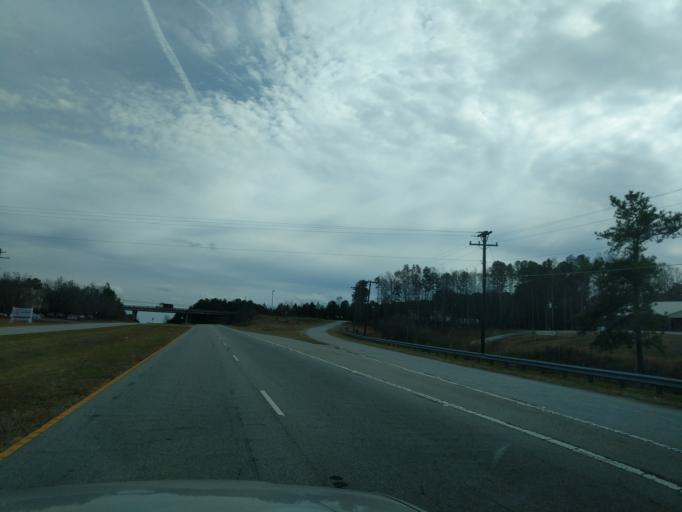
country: US
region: South Carolina
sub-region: Oconee County
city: Walhalla
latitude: 34.7433
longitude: -83.0376
